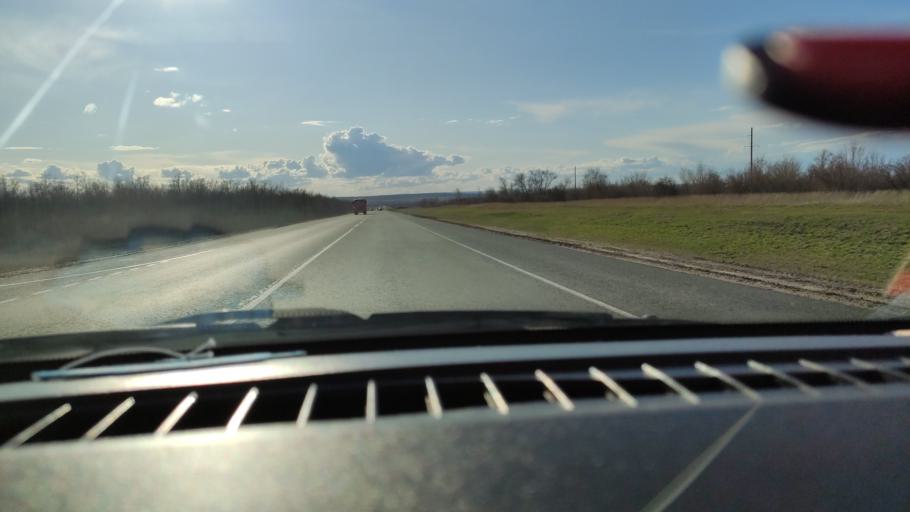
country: RU
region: Saratov
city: Yelshanka
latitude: 51.8270
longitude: 46.2742
